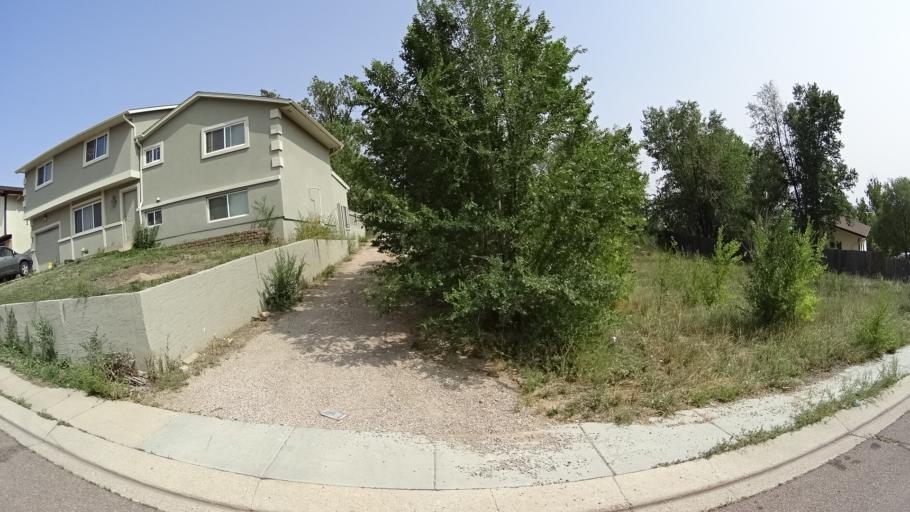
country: US
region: Colorado
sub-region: El Paso County
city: Stratmoor
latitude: 38.7980
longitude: -104.7709
